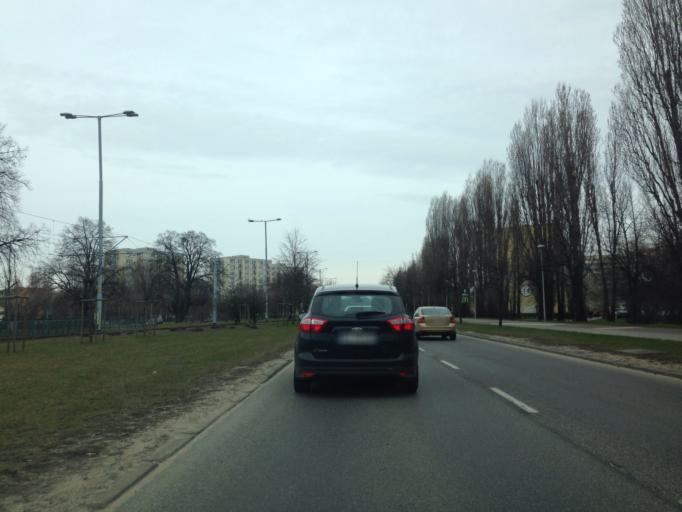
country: PL
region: Pomeranian Voivodeship
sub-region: Sopot
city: Sopot
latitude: 54.4044
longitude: 18.5914
